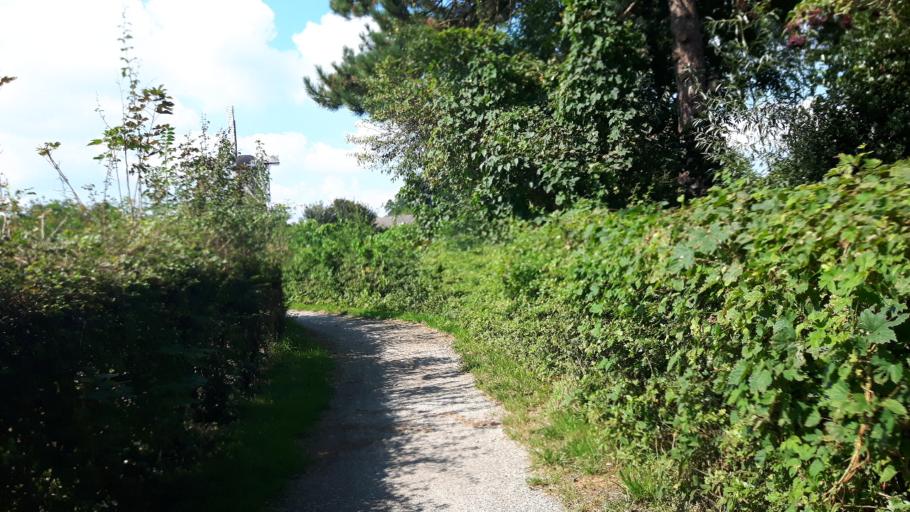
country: NL
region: Groningen
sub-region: Gemeente Groningen
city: Groningen
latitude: 53.1476
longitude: 6.4941
